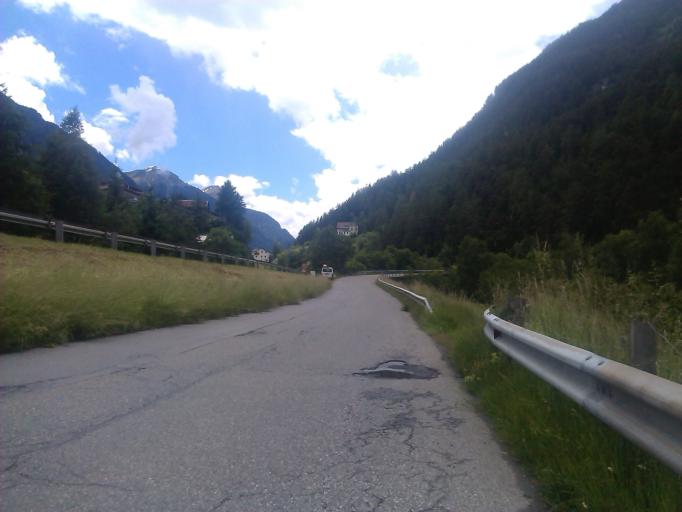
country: AT
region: Tyrol
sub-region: Politischer Bezirk Landeck
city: Serfaus
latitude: 47.0142
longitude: 10.6019
